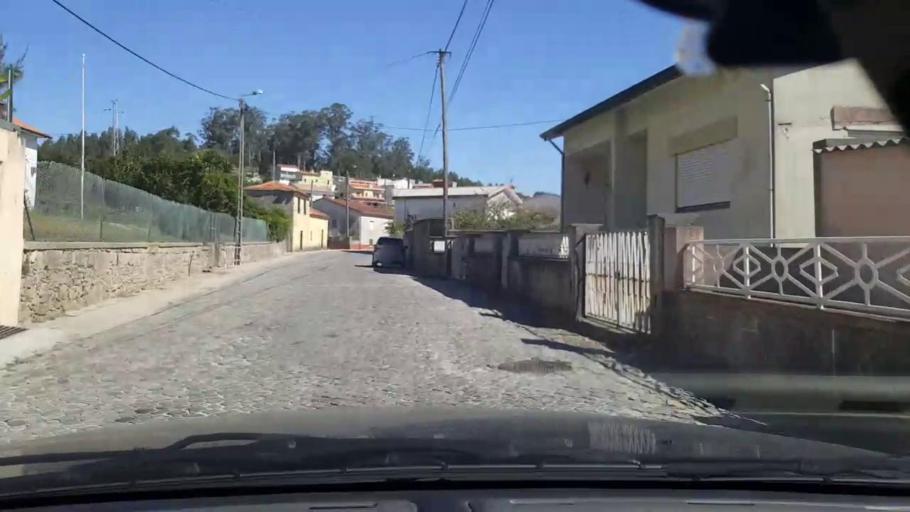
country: PT
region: Porto
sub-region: Maia
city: Gemunde
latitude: 41.3140
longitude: -8.6484
